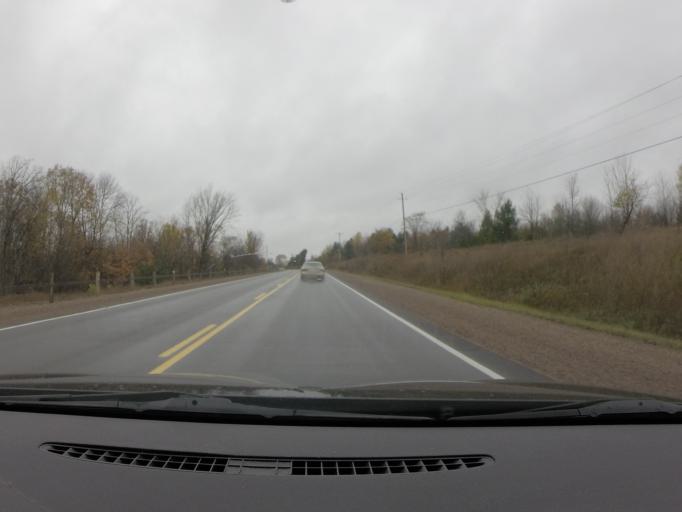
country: CA
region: Ontario
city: Skatepark
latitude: 44.7007
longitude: -77.0115
